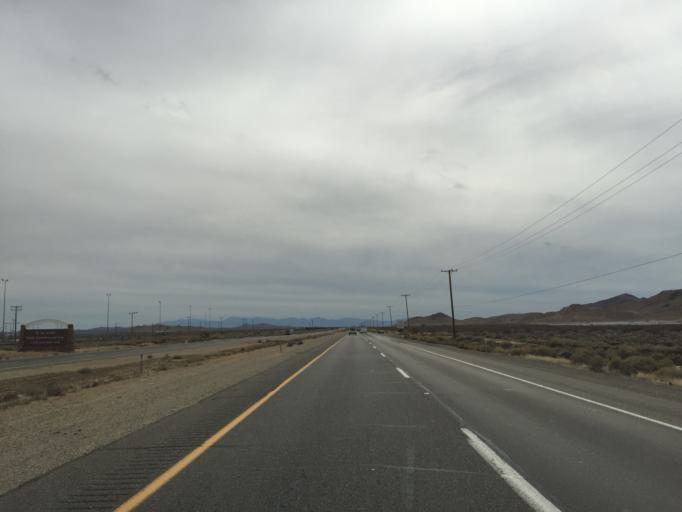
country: US
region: California
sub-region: Kern County
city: Mojave
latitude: 35.0297
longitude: -118.1676
